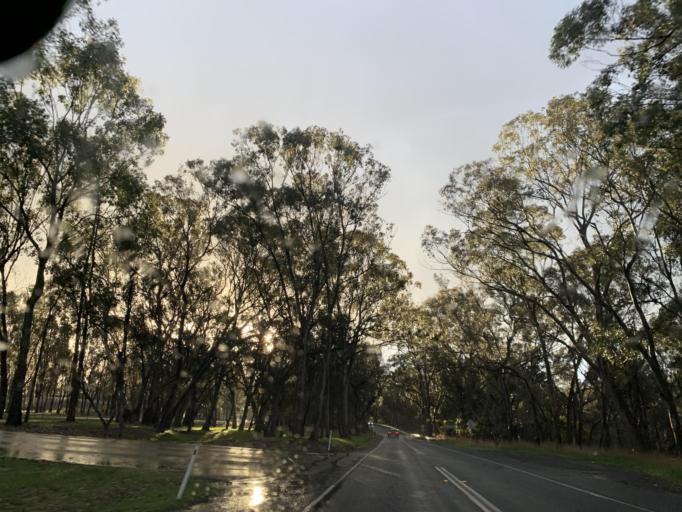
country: AU
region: Victoria
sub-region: Murrindindi
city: Kinglake West
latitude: -37.2082
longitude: 145.0831
